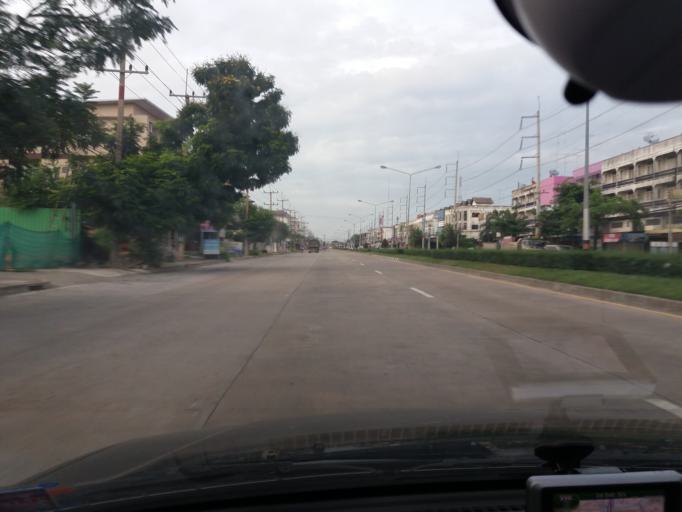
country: TH
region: Suphan Buri
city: U Thong
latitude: 14.3829
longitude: 99.8946
